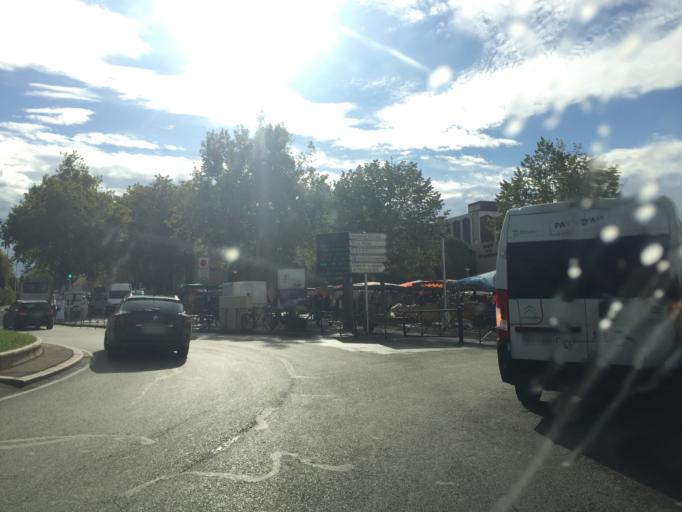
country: FR
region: Provence-Alpes-Cote d'Azur
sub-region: Departement des Bouches-du-Rhone
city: Aix-en-Provence
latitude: 43.5241
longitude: 5.4331
